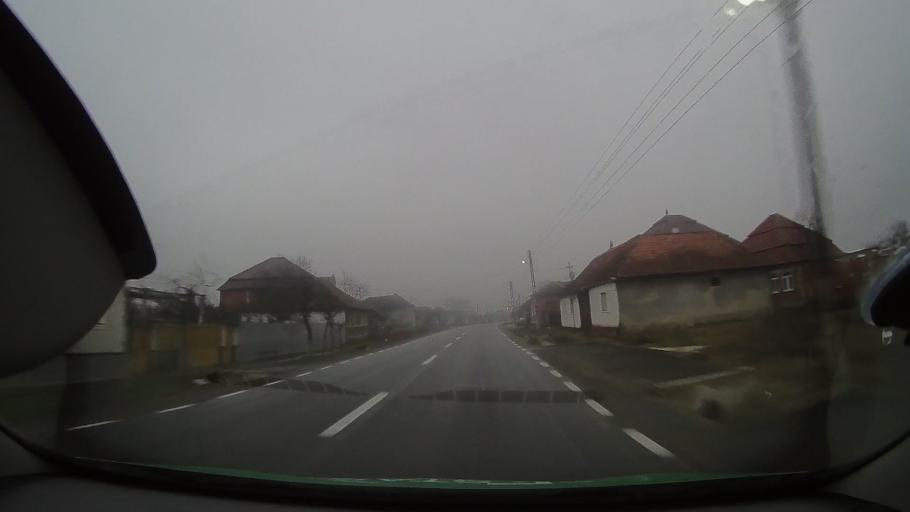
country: RO
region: Bihor
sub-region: Comuna Olcea
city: Calacea
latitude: 46.6336
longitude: 21.9574
